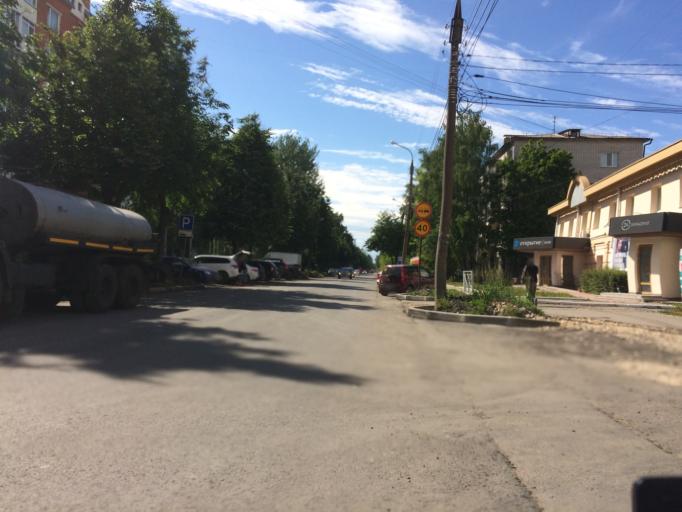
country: RU
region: Mariy-El
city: Yoshkar-Ola
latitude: 56.6445
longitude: 47.8983
